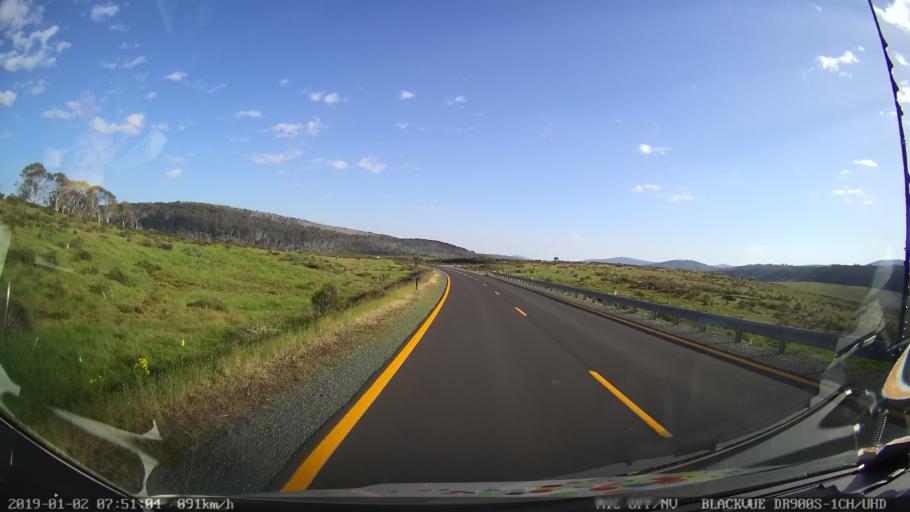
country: AU
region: New South Wales
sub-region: Tumut Shire
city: Tumut
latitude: -35.7228
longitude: 148.5308
